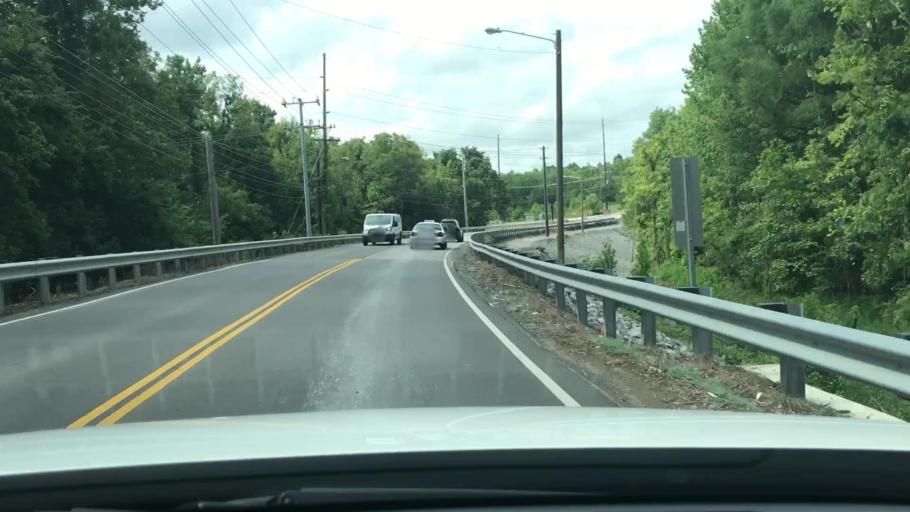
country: US
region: Tennessee
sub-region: Davidson County
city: Oak Hill
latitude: 36.0946
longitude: -86.6899
